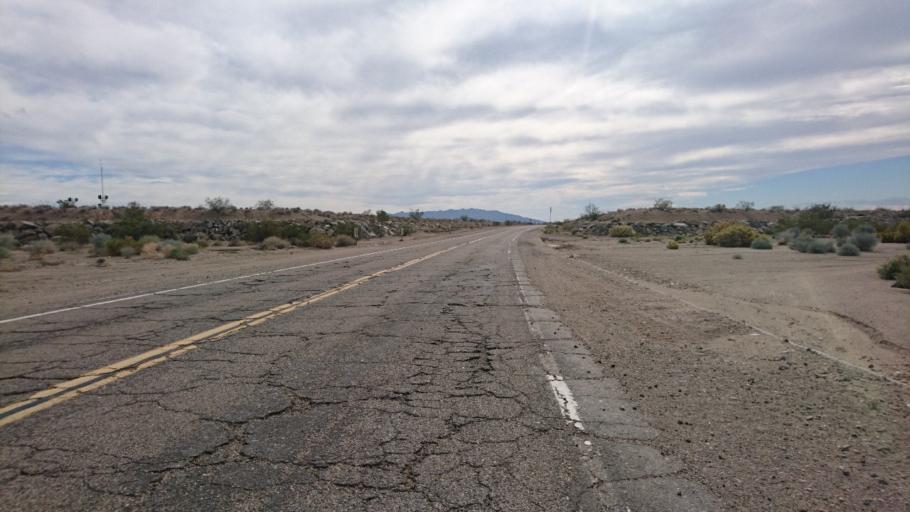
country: US
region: California
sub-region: San Bernardino County
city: Needles
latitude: 34.8066
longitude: -115.1915
